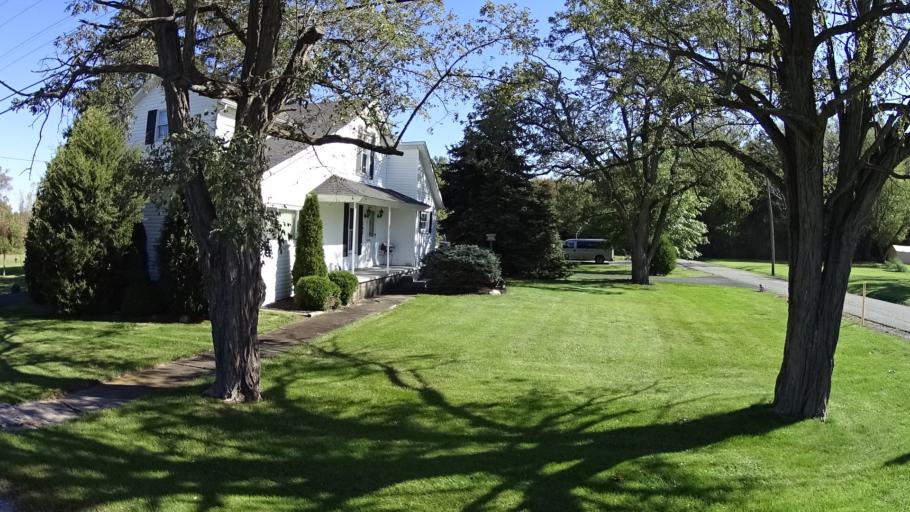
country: US
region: Ohio
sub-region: Lorain County
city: South Amherst
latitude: 41.3820
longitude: -82.2524
